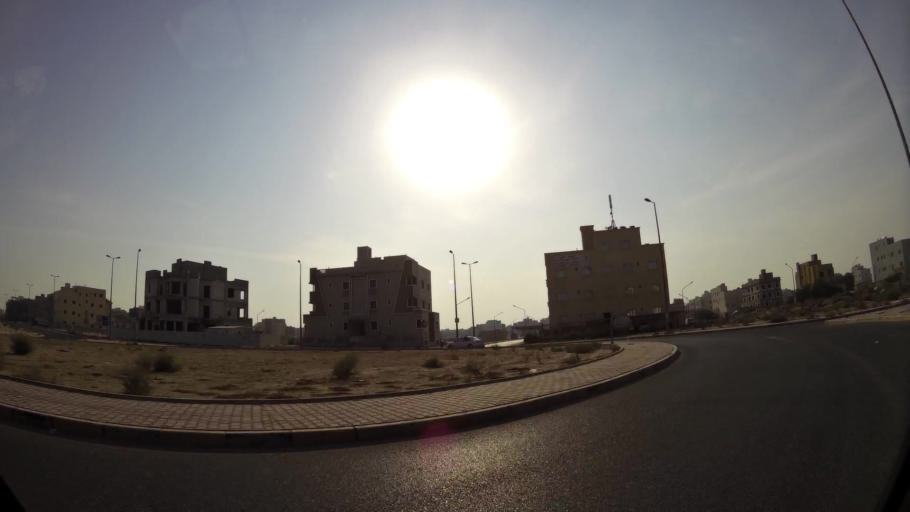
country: KW
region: Mubarak al Kabir
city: Mubarak al Kabir
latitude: 29.1920
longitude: 48.1060
